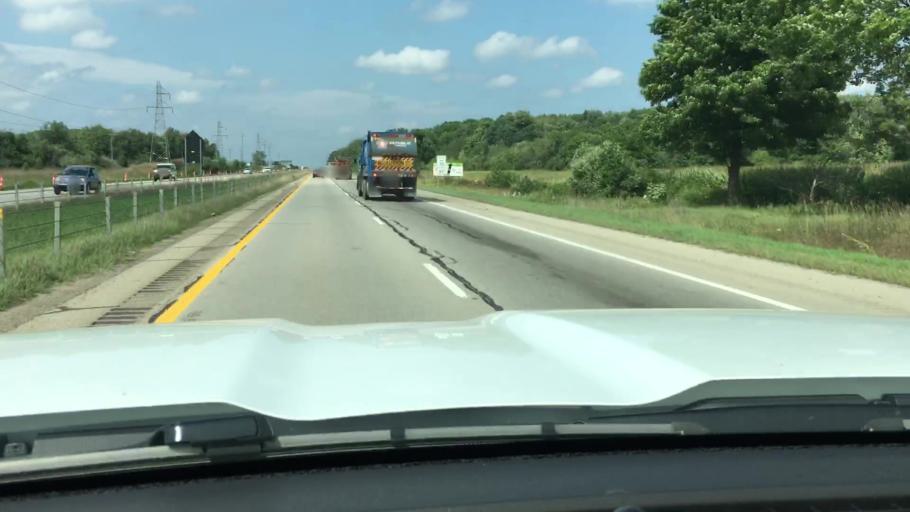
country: US
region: Michigan
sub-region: Kent County
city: Cutlerville
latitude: 42.7905
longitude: -85.6683
